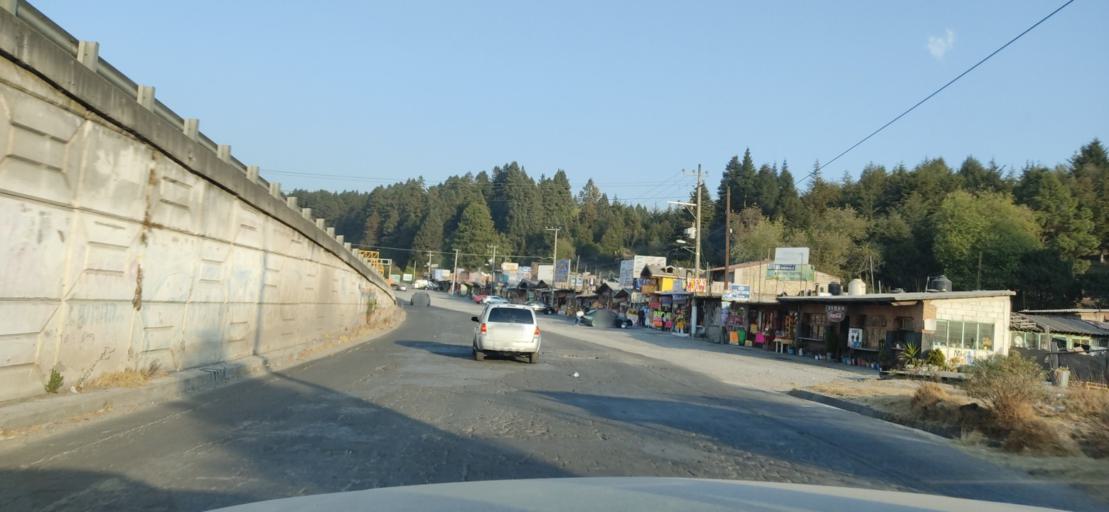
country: MX
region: Mexico
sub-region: Ocoyoacac
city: San Jeronimo Acazulco
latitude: 19.2978
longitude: -99.3715
